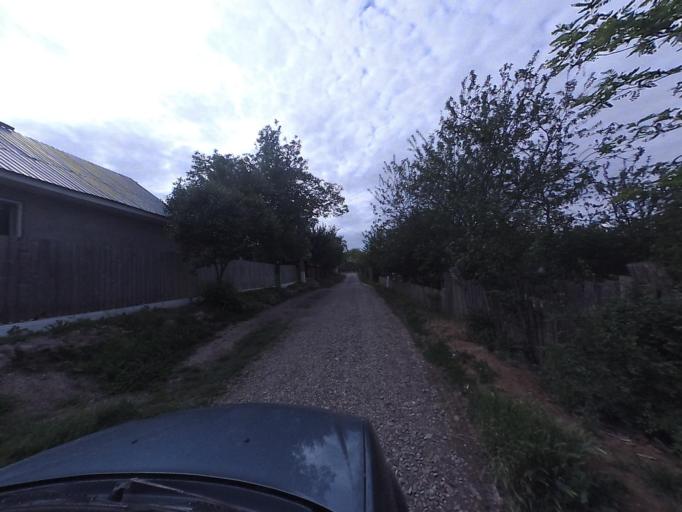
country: RO
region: Neamt
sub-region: Comuna Dulcesti
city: Dulcesti
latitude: 46.9593
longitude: 26.7859
